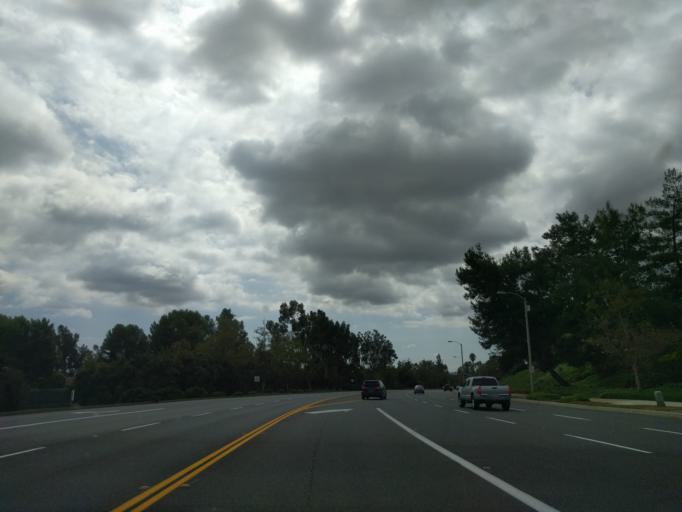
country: US
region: California
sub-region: Orange County
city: Lake Forest
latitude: 33.6397
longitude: -117.6712
